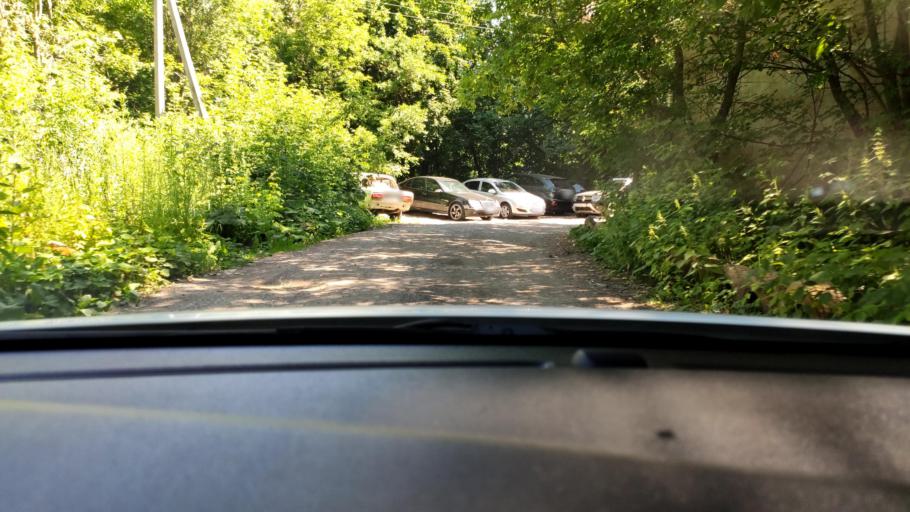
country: RU
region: Tatarstan
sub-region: Gorod Kazan'
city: Kazan
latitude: 55.7579
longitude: 49.2000
